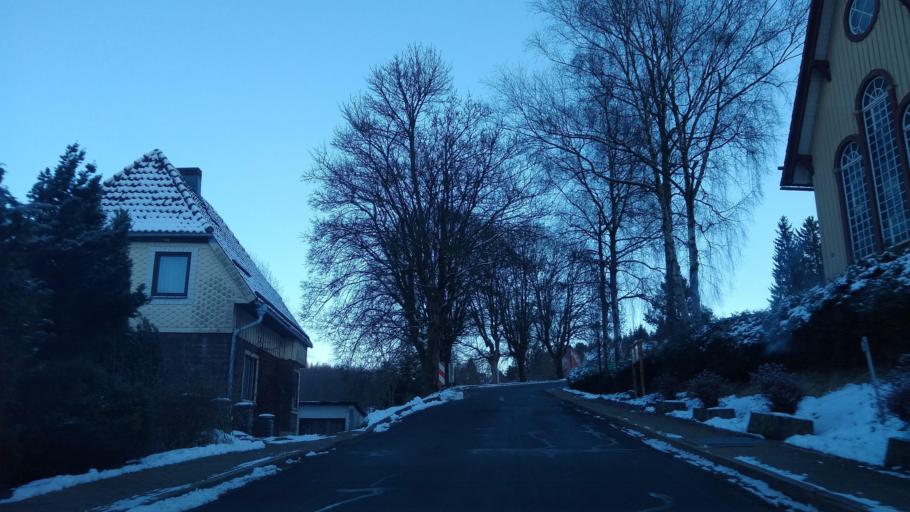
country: DE
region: Saxony-Anhalt
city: Benneckenstein
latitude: 51.6938
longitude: 10.6977
